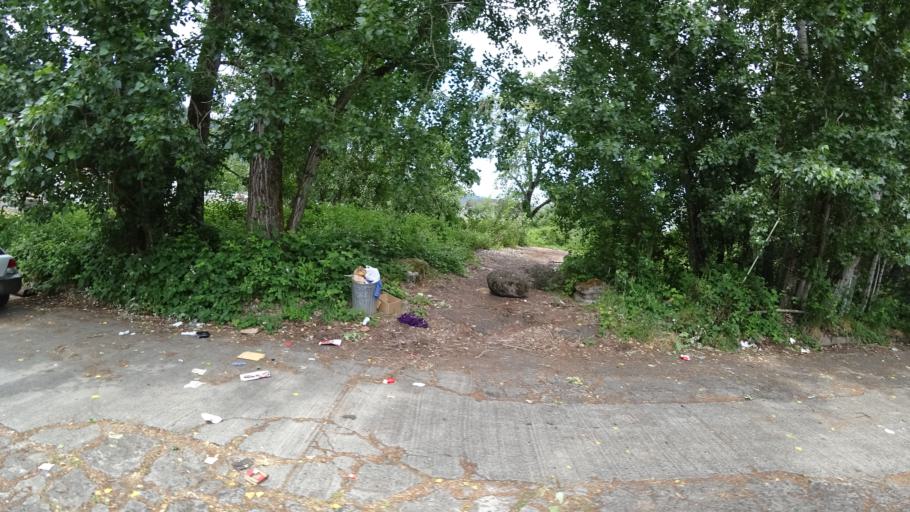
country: US
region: Oregon
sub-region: Washington County
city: West Haven
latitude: 45.5839
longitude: -122.7544
